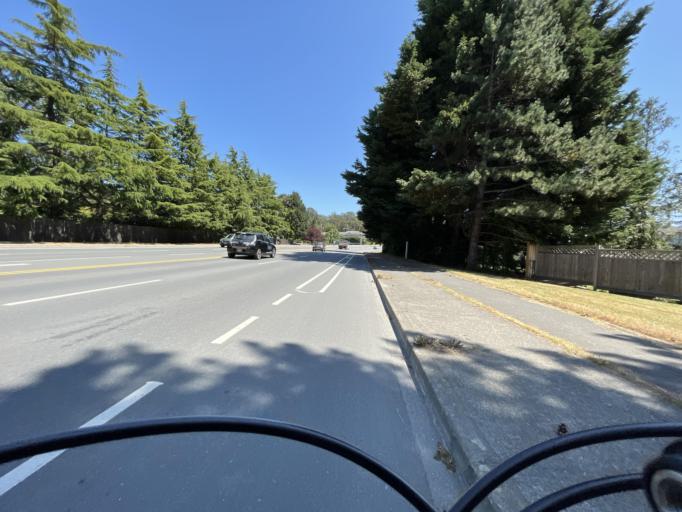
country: CA
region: British Columbia
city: Victoria
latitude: 48.4718
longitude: -123.3463
